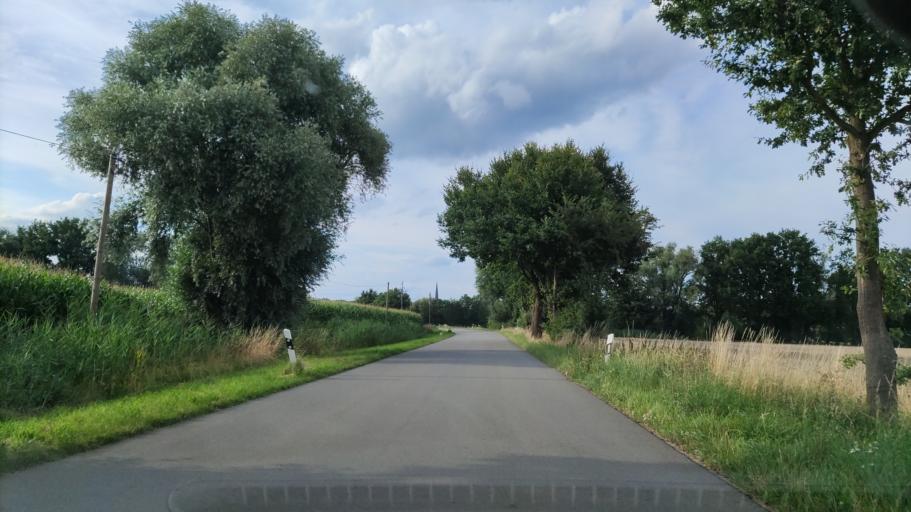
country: DE
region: Lower Saxony
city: Dannenberg
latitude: 53.0917
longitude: 11.0981
